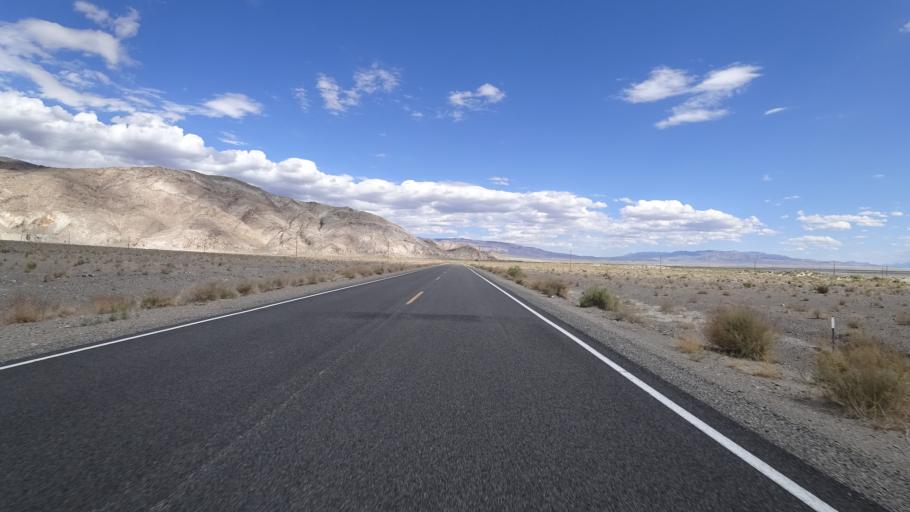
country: US
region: California
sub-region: Inyo County
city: Lone Pine
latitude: 36.5427
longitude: -117.9345
